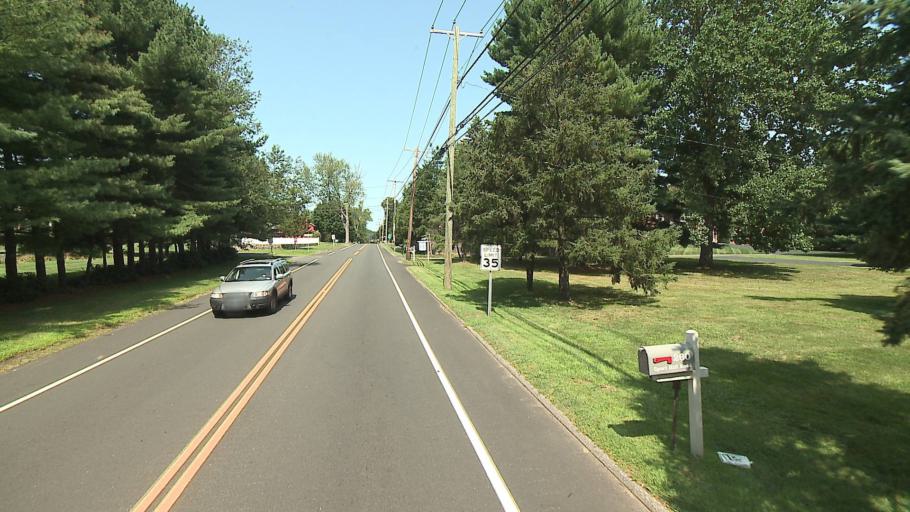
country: US
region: Connecticut
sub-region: Fairfield County
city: Trumbull
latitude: 41.2374
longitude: -73.2684
